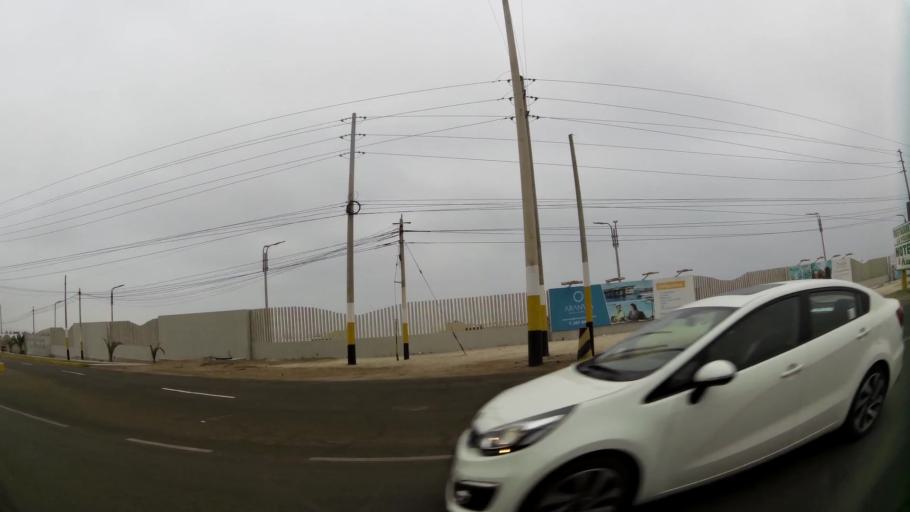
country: PE
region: Ica
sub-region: Provincia de Pisco
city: Paracas
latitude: -13.8273
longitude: -76.2447
